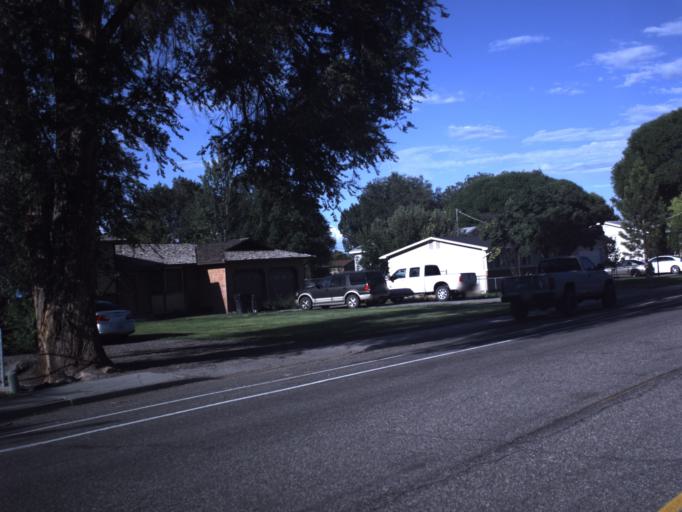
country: US
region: Utah
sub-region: Sevier County
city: Monroe
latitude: 38.6830
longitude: -112.1442
